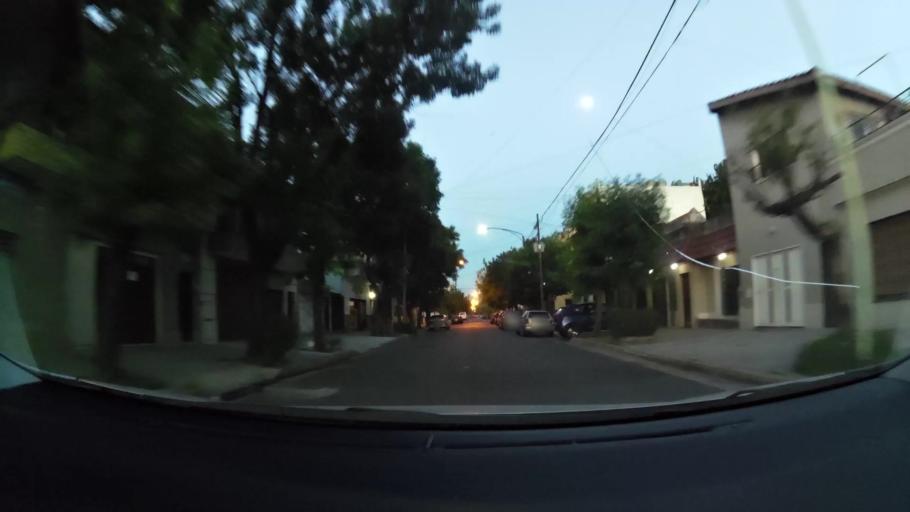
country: AR
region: Buenos Aires F.D.
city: Villa Lugano
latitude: -34.6924
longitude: -58.4720
